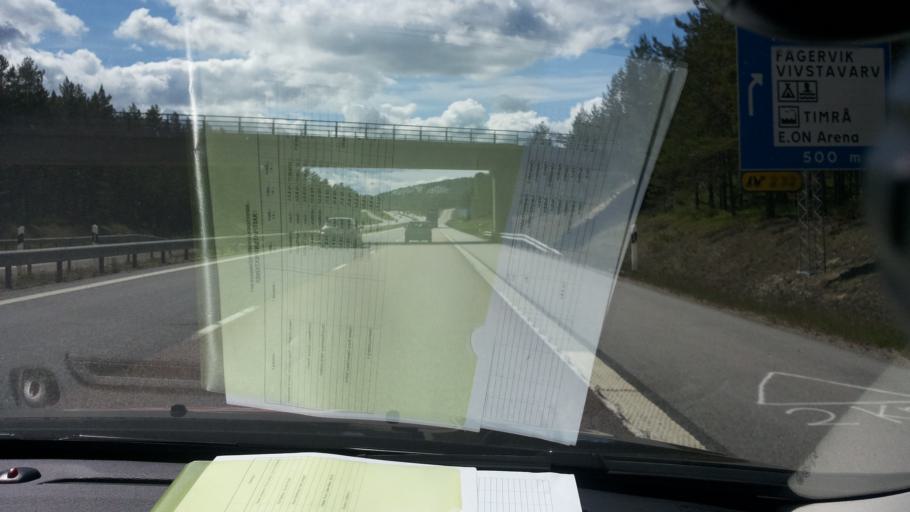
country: SE
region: Vaesternorrland
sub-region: Timra Kommun
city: Timra
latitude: 62.5030
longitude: 17.3495
